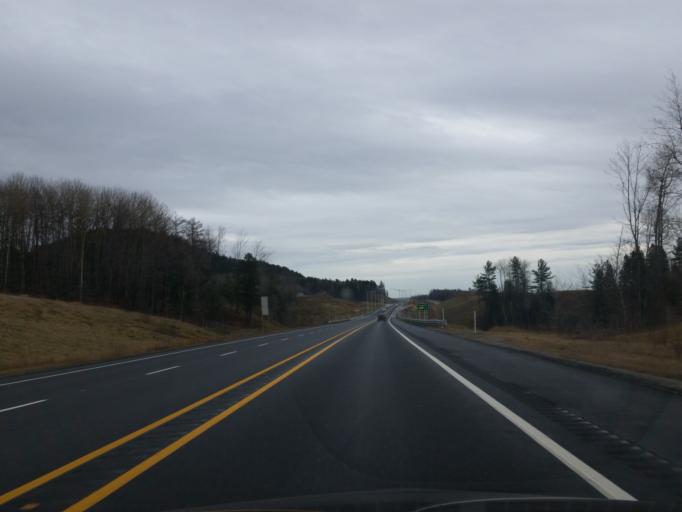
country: CA
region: Quebec
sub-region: Outaouais
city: Papineauville
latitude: 45.6626
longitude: -74.8809
